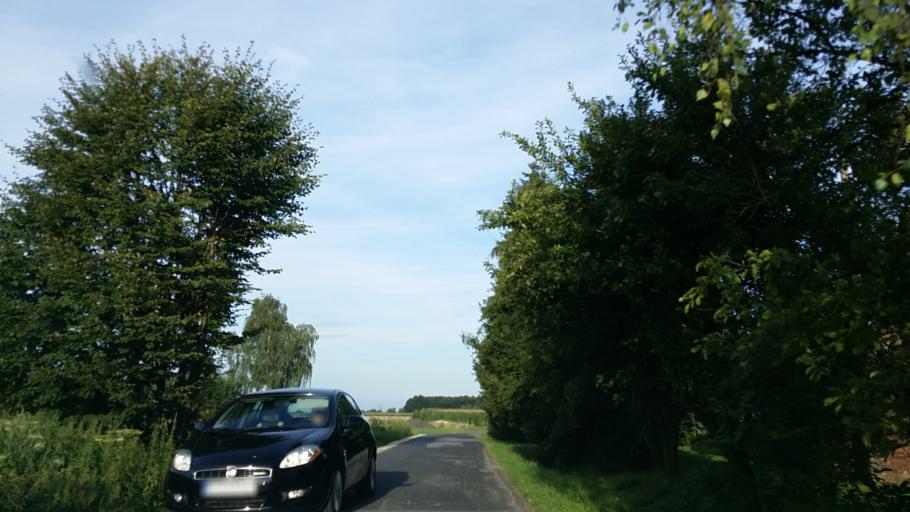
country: PL
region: Lesser Poland Voivodeship
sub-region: Powiat oswiecimski
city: Przeciszow
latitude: 49.9915
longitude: 19.4005
